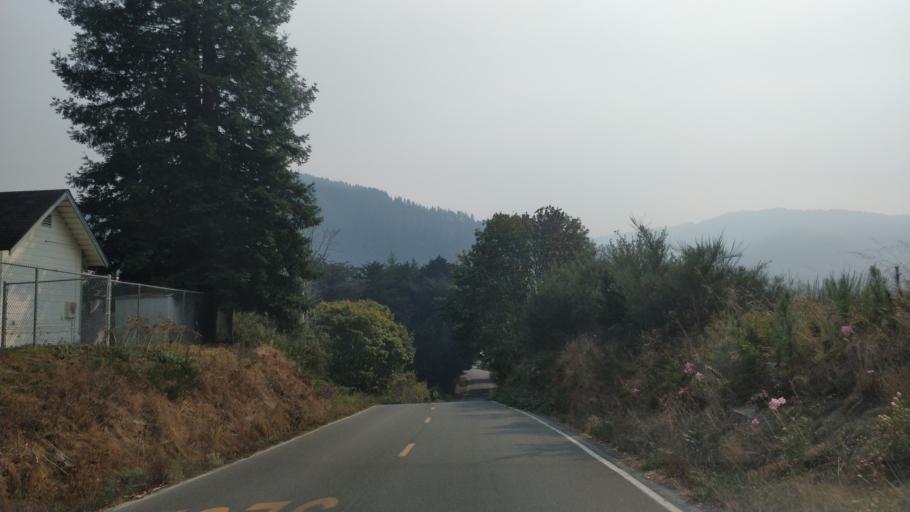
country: US
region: California
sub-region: Humboldt County
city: Rio Dell
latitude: 40.3220
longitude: -124.2858
